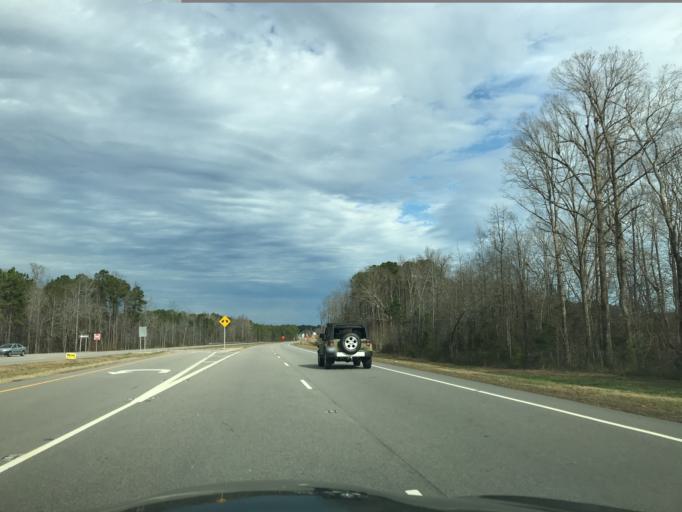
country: US
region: North Carolina
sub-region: Wake County
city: Rolesville
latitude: 35.9299
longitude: -78.4355
